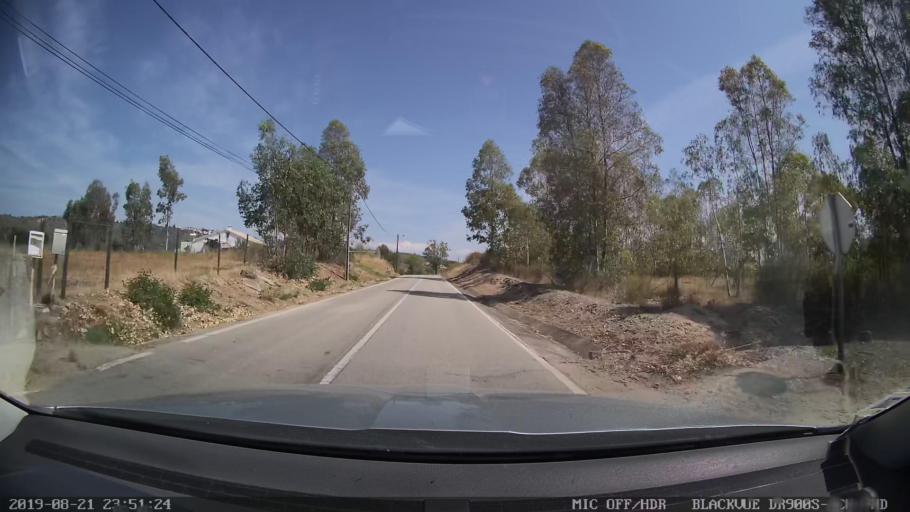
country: PT
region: Castelo Branco
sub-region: Idanha-A-Nova
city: Idanha-a-Nova
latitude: 39.9014
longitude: -7.2348
